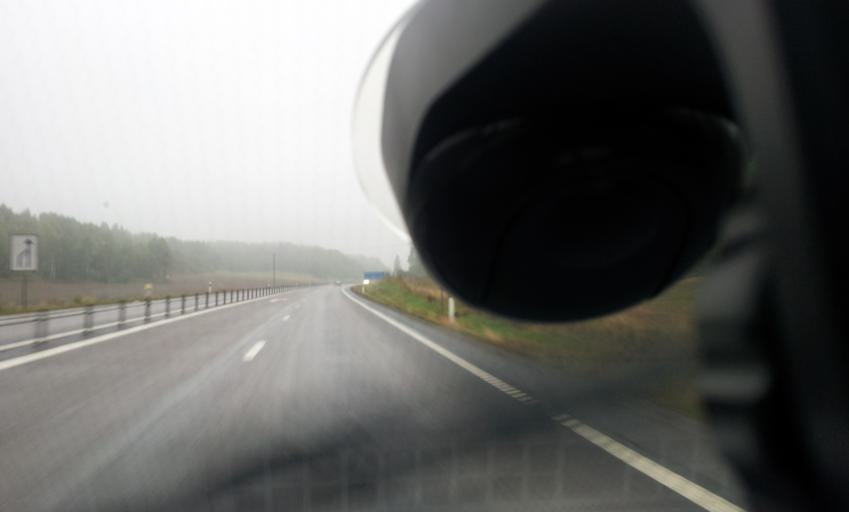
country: SE
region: OEstergoetland
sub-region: Valdemarsviks Kommun
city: Gusum
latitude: 58.3128
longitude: 16.4815
